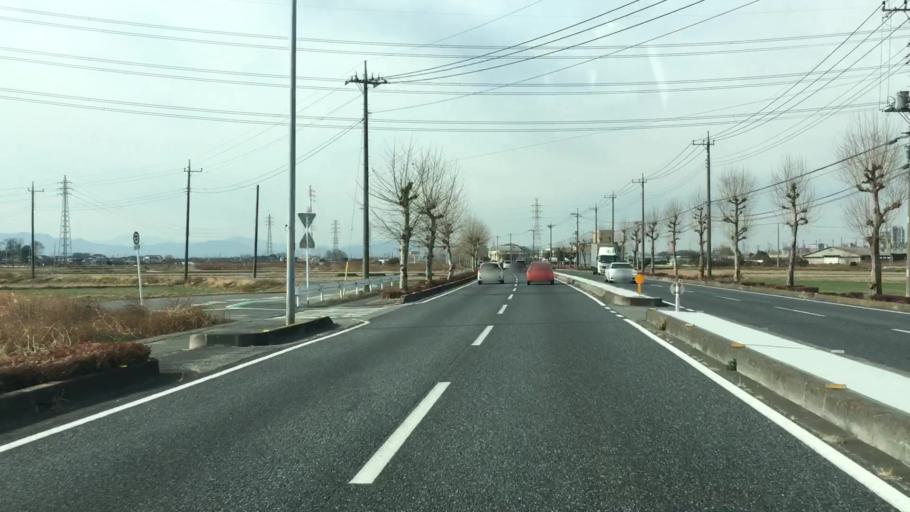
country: JP
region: Saitama
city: Kumagaya
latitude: 36.1505
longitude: 139.3380
